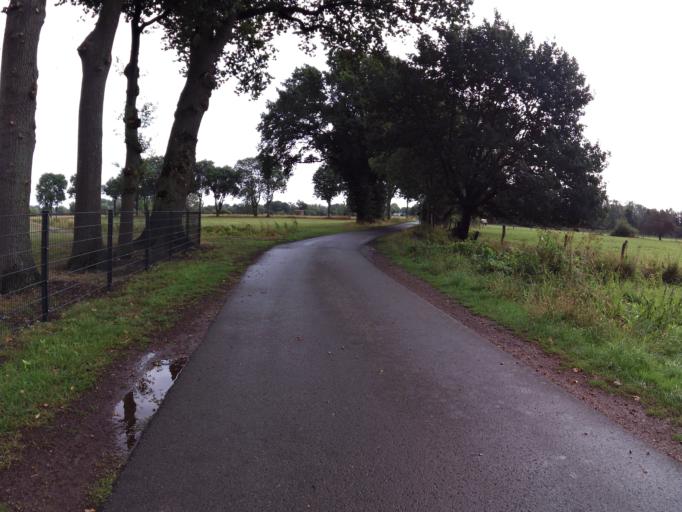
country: DE
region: Lower Saxony
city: Marklohe
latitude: 52.6883
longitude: 9.1697
